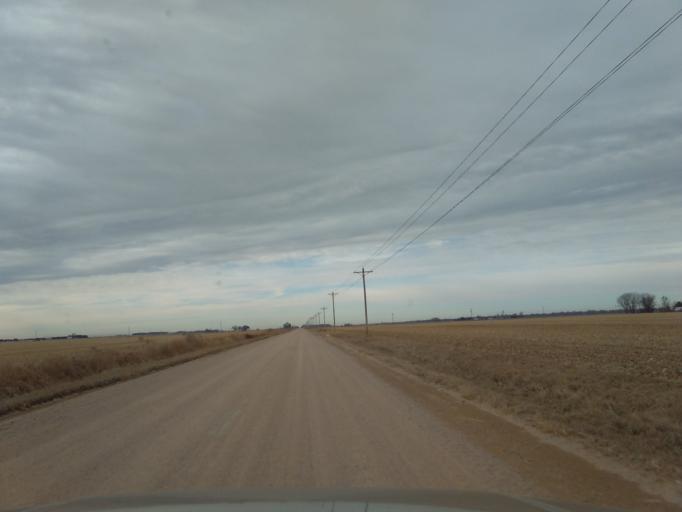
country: US
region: Nebraska
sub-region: Buffalo County
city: Gibbon
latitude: 40.6408
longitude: -98.9069
